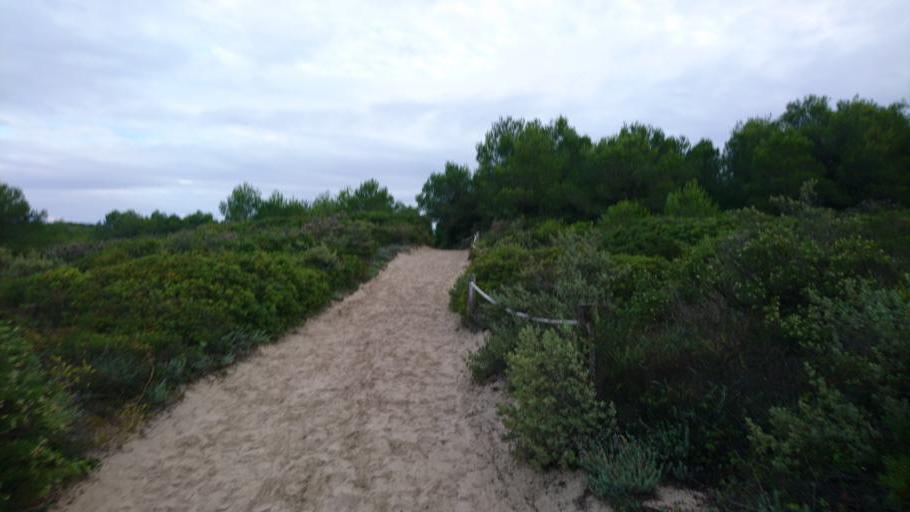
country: ES
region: Balearic Islands
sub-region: Illes Balears
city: Port d'Alcudia
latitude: 39.7765
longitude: 3.1386
